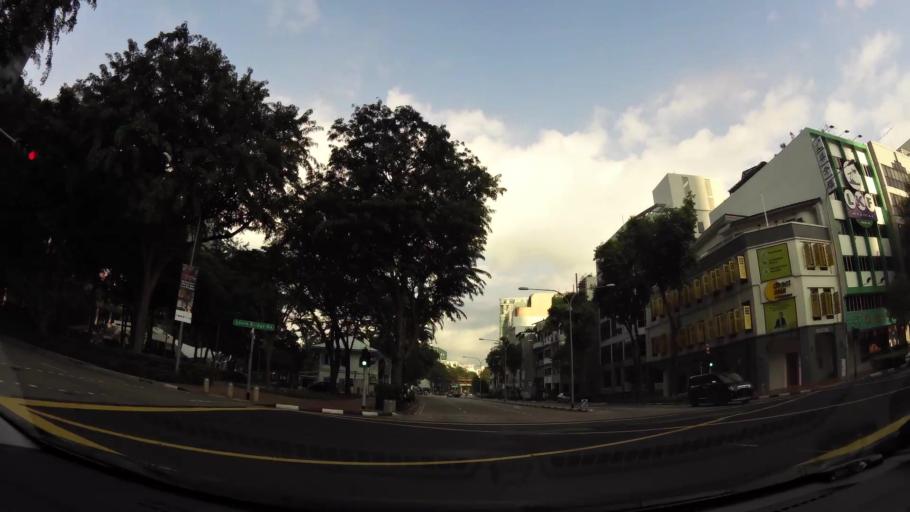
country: SG
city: Singapore
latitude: 1.2864
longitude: 103.8477
